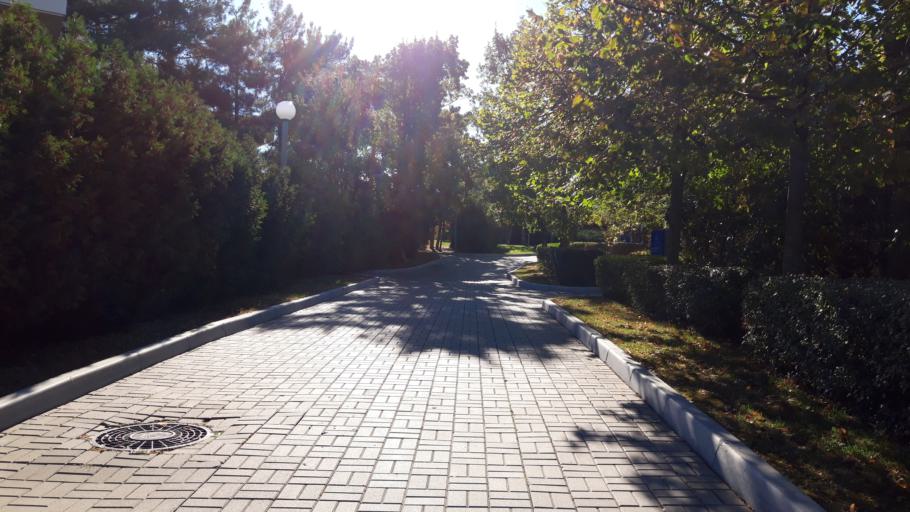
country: RU
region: Krasnodarskiy
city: Gelendzhik
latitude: 44.5529
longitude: 38.0540
